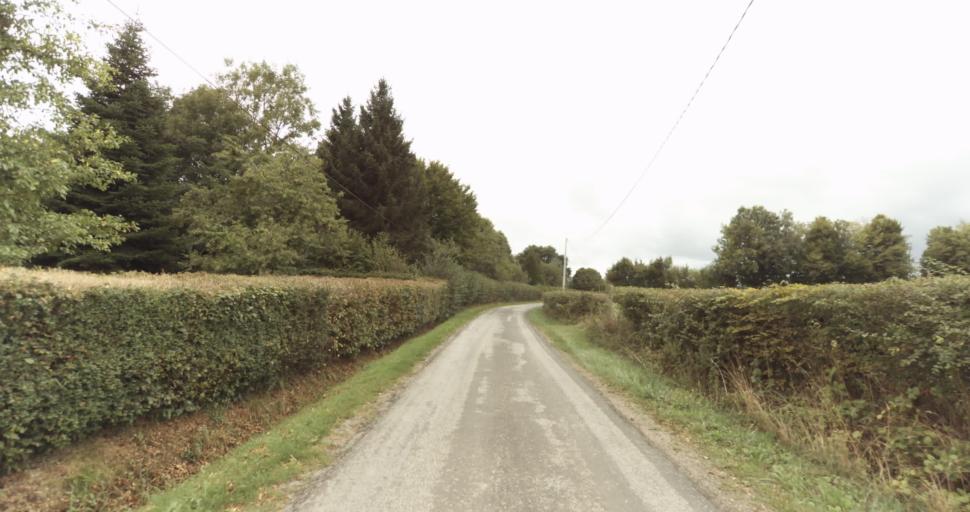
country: FR
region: Lower Normandy
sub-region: Departement de l'Orne
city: Sainte-Gauburge-Sainte-Colombe
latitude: 48.7083
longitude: 0.3475
